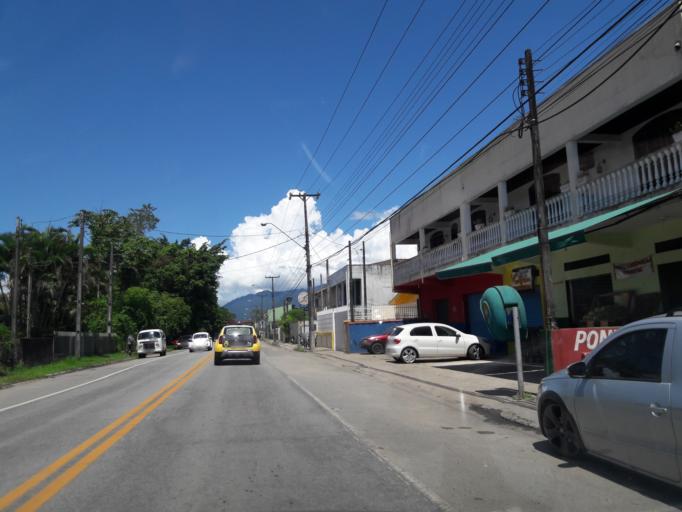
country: BR
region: Parana
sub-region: Antonina
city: Antonina
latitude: -25.4832
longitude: -48.8288
